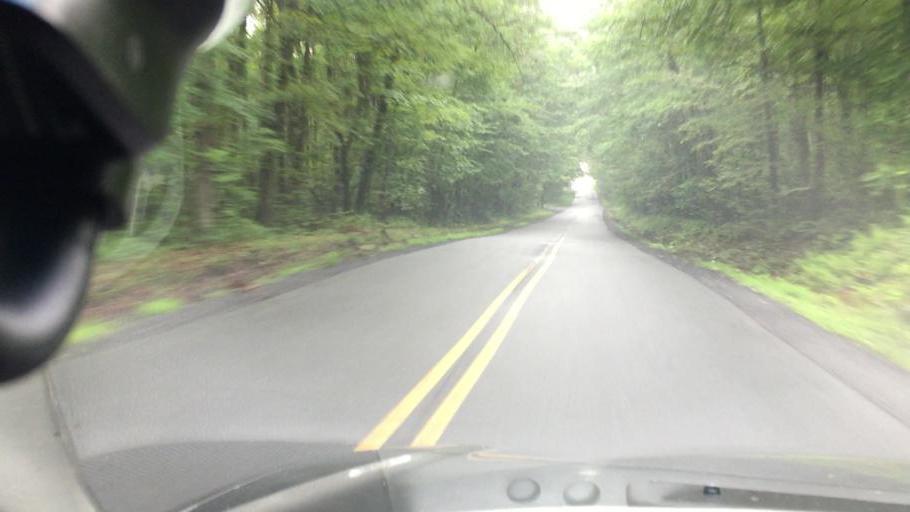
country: US
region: Pennsylvania
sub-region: Luzerne County
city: Freeland
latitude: 41.0234
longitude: -75.9088
